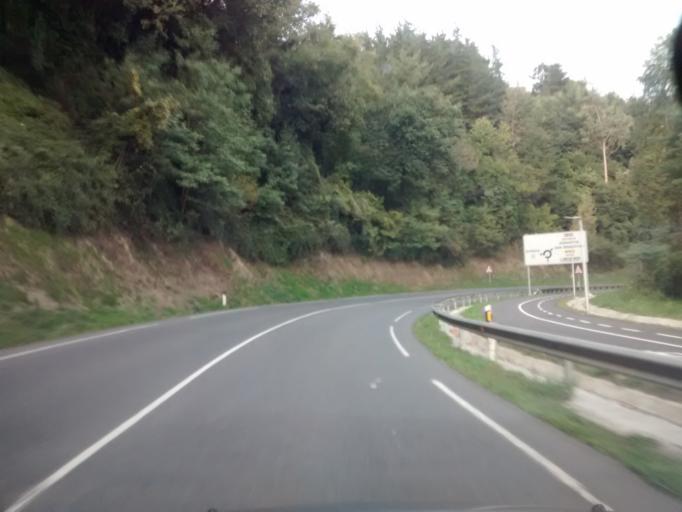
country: ES
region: Basque Country
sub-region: Provincia de Guipuzcoa
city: Zumaia
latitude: 43.2852
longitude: -2.2628
